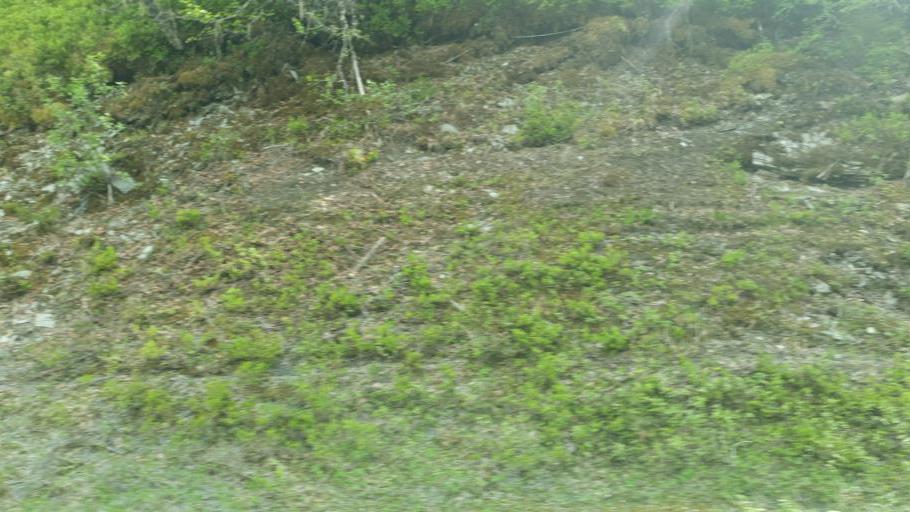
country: NO
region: Nord-Trondelag
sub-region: Leksvik
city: Leksvik
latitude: 63.6941
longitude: 10.4688
